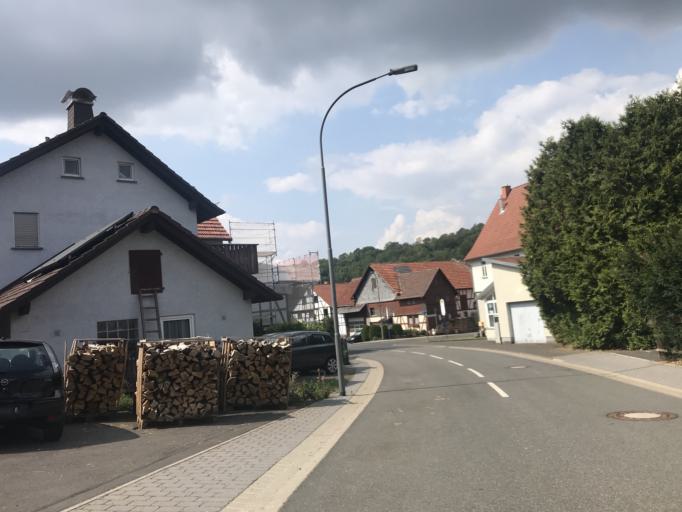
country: DE
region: Hesse
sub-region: Regierungsbezirk Giessen
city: Ulrichstein
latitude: 50.5740
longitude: 9.1245
